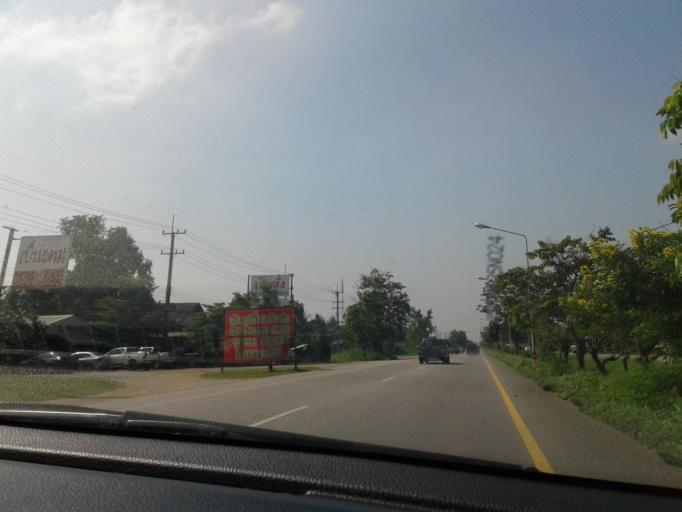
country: TH
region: Ratchaburi
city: Ban Pong
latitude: 13.7791
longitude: 99.9366
